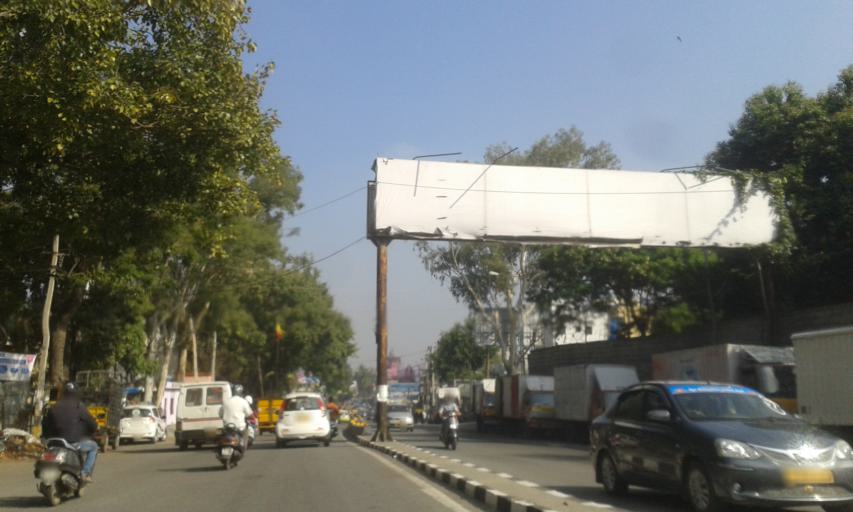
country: IN
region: Karnataka
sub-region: Bangalore Urban
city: Bangalore
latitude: 12.9393
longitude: 77.6021
